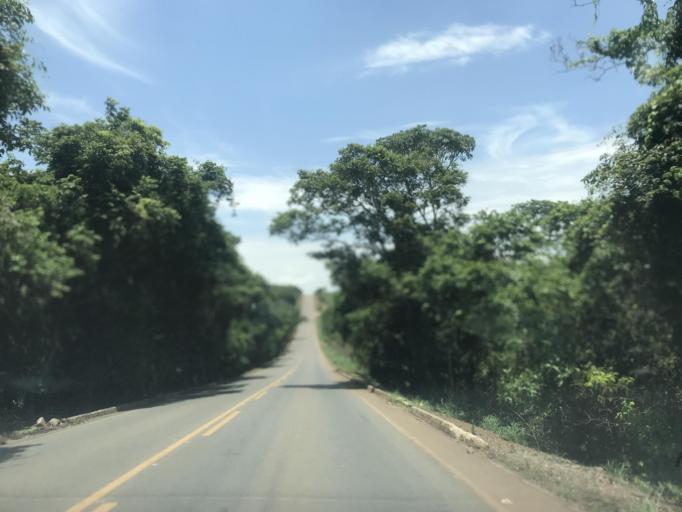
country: BR
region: Goias
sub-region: Vianopolis
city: Vianopolis
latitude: -16.6109
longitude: -48.3511
